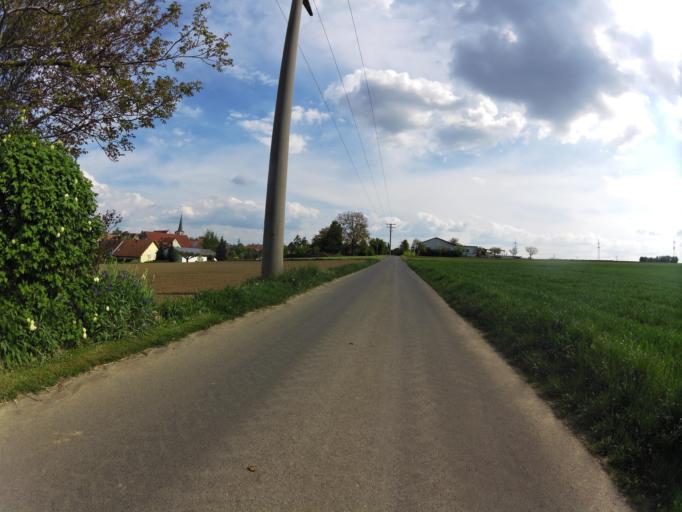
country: DE
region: Bavaria
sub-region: Regierungsbezirk Unterfranken
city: Giebelstadt
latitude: 49.6124
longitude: 9.9459
